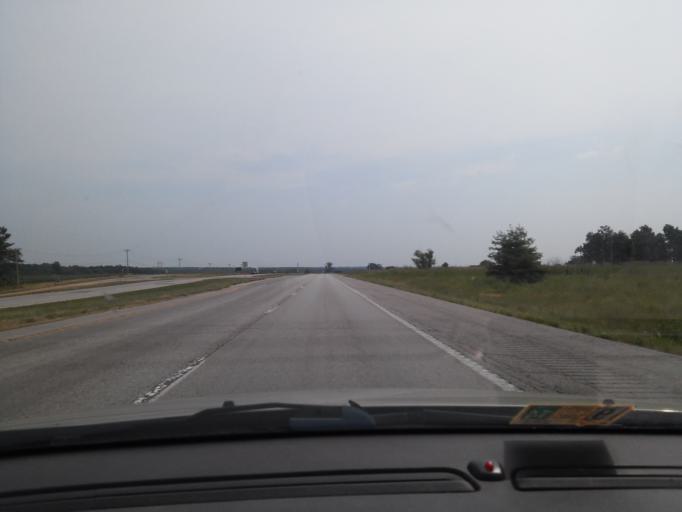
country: US
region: Missouri
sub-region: Callaway County
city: Fulton
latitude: 38.9646
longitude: -91.9105
